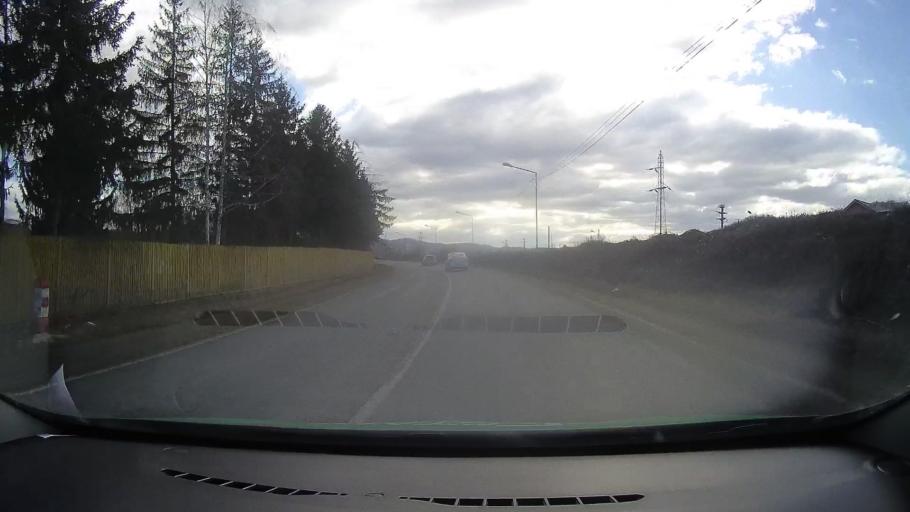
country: RO
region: Dambovita
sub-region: Oras Pucioasa
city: Pucioasa
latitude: 45.0841
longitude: 25.4216
